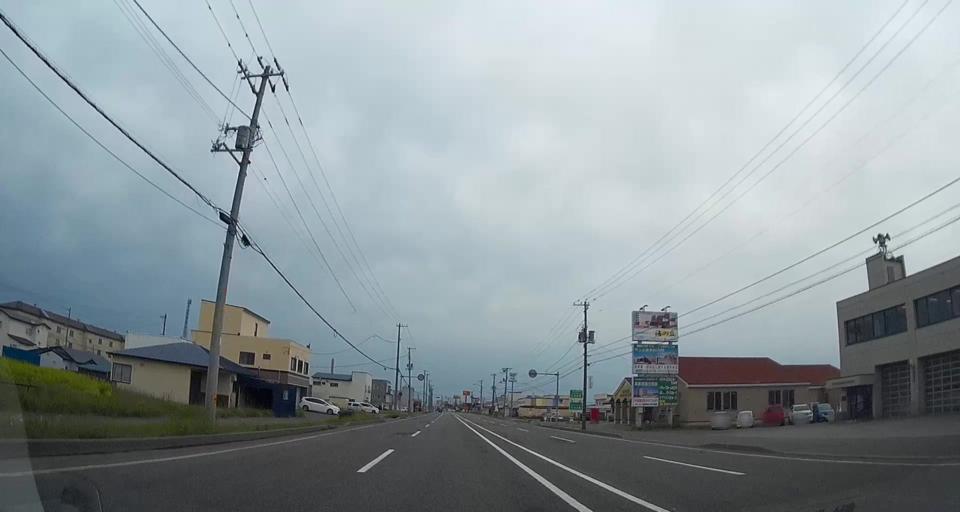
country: JP
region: Hokkaido
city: Tomakomai
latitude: 42.6240
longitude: 141.5765
